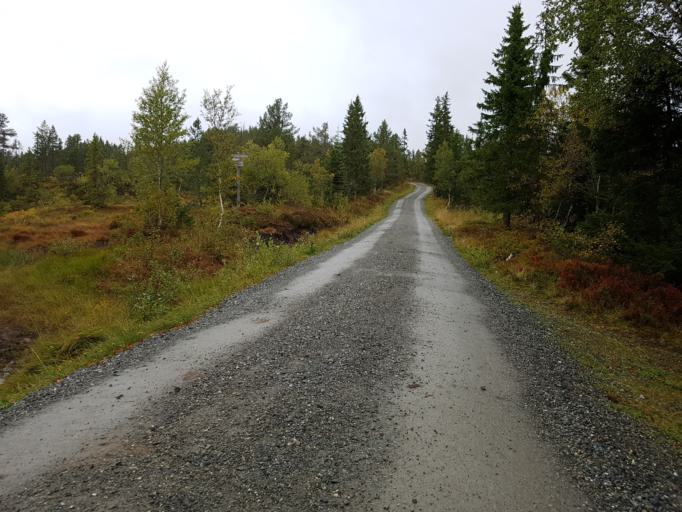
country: NO
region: Sor-Trondelag
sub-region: Melhus
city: Melhus
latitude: 63.4140
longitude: 10.2466
